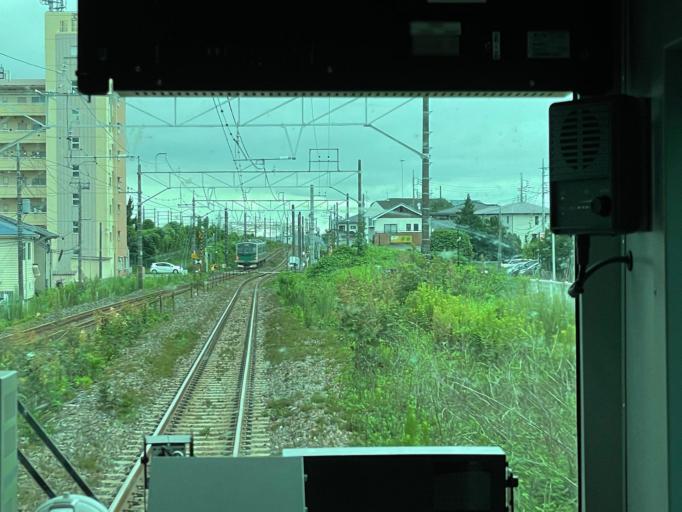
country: JP
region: Tochigi
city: Utsunomiya-shi
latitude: 36.5970
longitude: 139.9424
